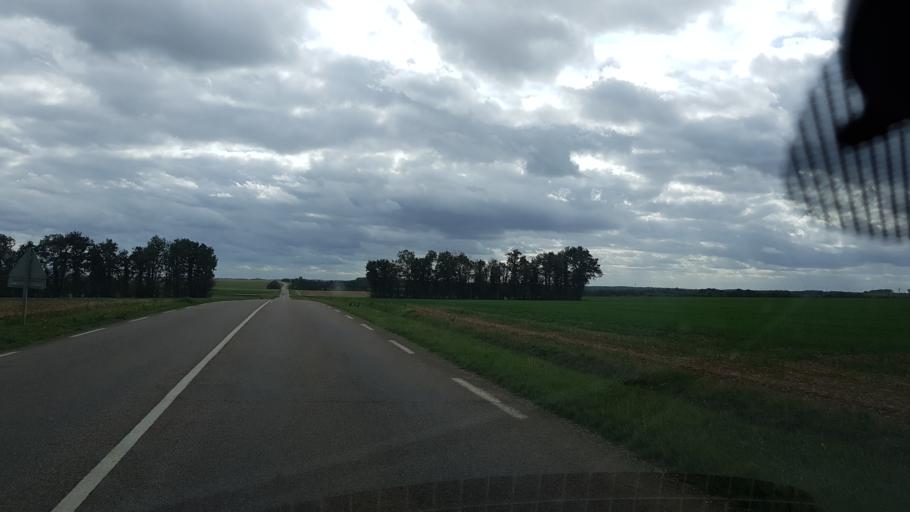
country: FR
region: Ile-de-France
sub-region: Departement de l'Essonne
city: Saclas
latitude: 48.3839
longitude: 2.1689
